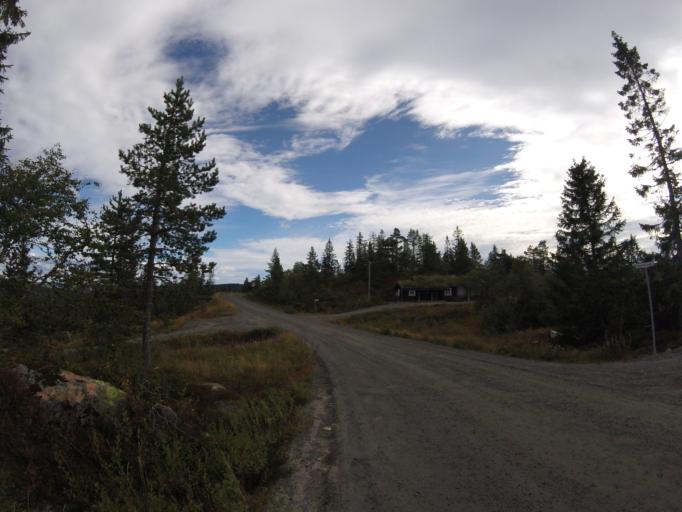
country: NO
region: Buskerud
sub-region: Flesberg
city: Lampeland
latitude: 59.7667
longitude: 9.4623
